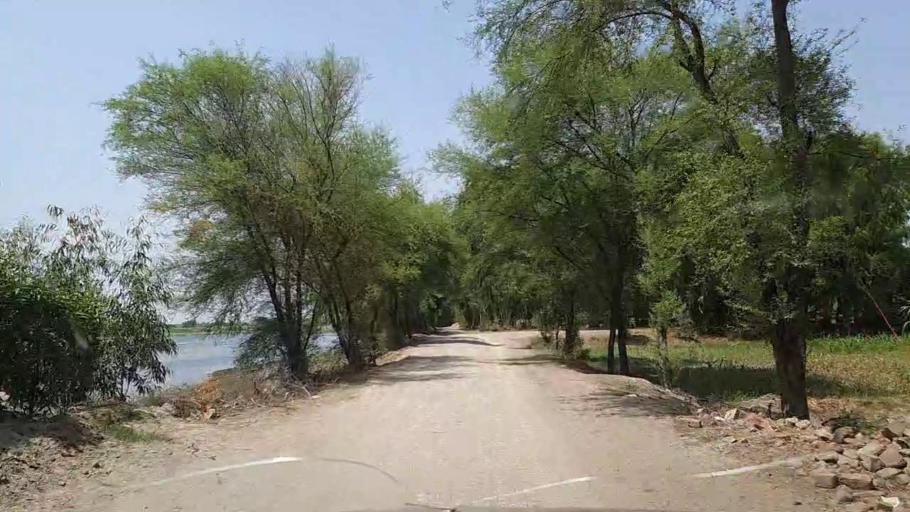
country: PK
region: Sindh
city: Ghotki
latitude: 28.0854
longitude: 69.3113
